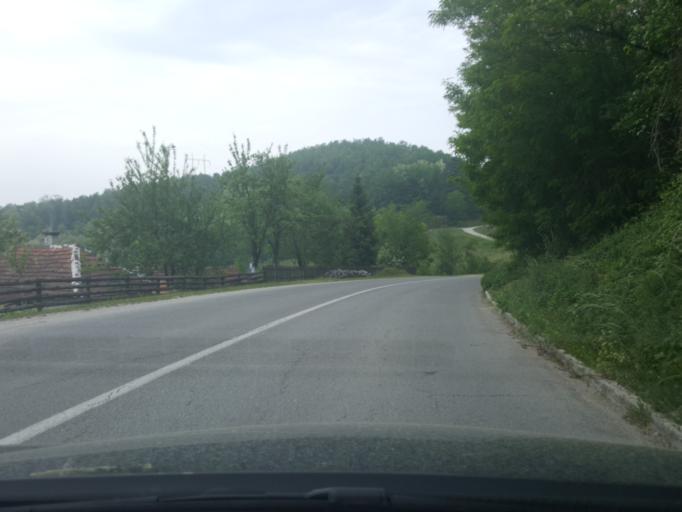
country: RS
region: Central Serbia
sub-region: Zlatiborski Okrug
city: Bajina Basta
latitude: 43.9426
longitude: 19.5670
